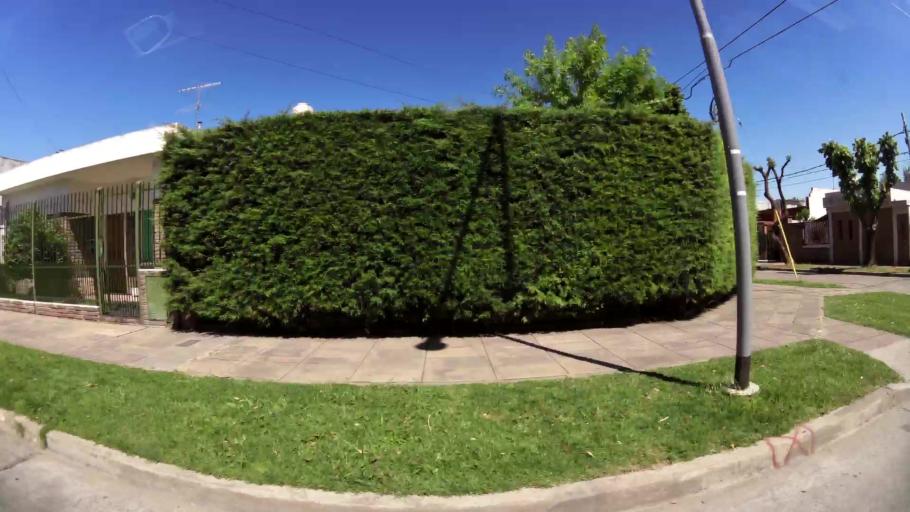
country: AR
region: Buenos Aires
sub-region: Partido de General San Martin
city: General San Martin
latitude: -34.5312
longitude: -58.5650
